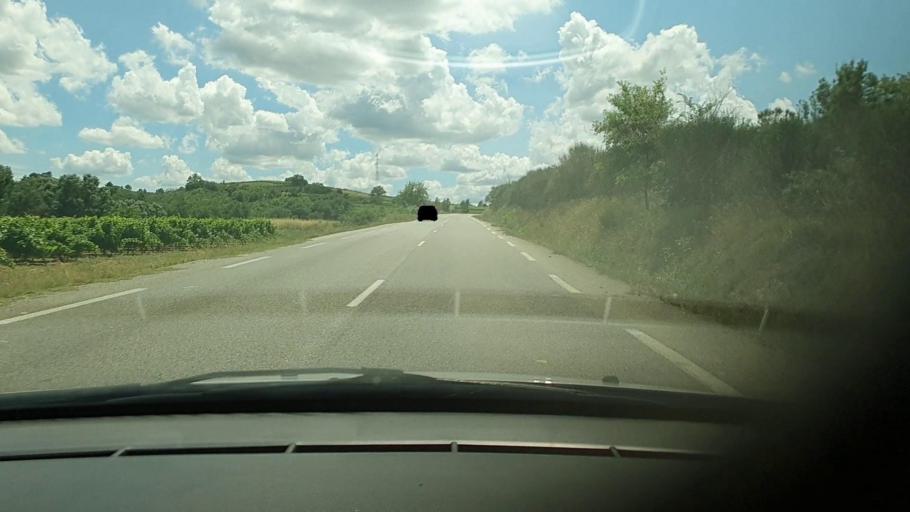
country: FR
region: Languedoc-Roussillon
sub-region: Departement du Gard
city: Mons
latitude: 44.0631
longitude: 4.2234
